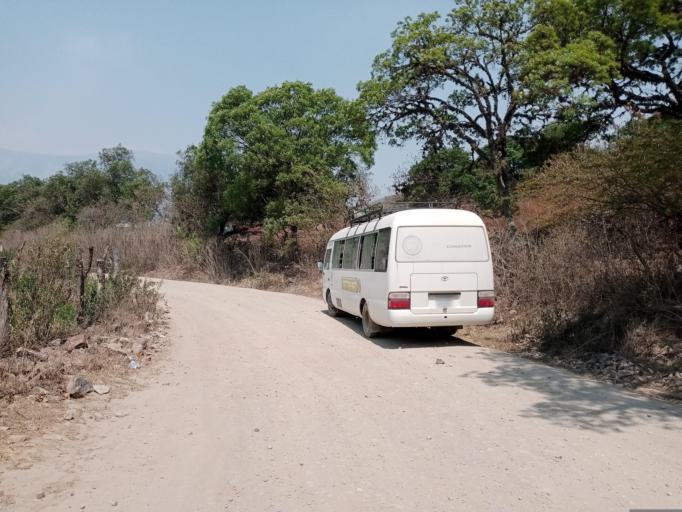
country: BO
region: La Paz
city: Quime
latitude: -16.8932
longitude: -67.1419
